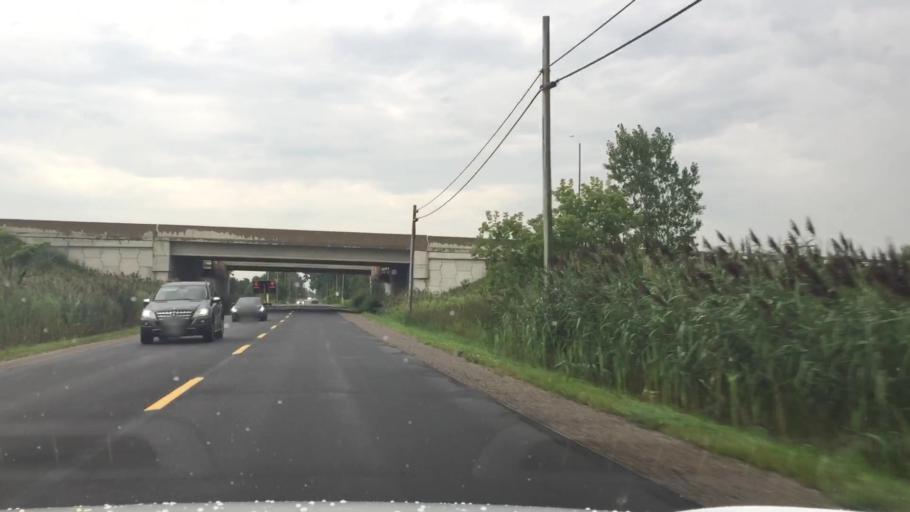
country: CA
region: Ontario
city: Markham
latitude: 43.8768
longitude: -79.2087
